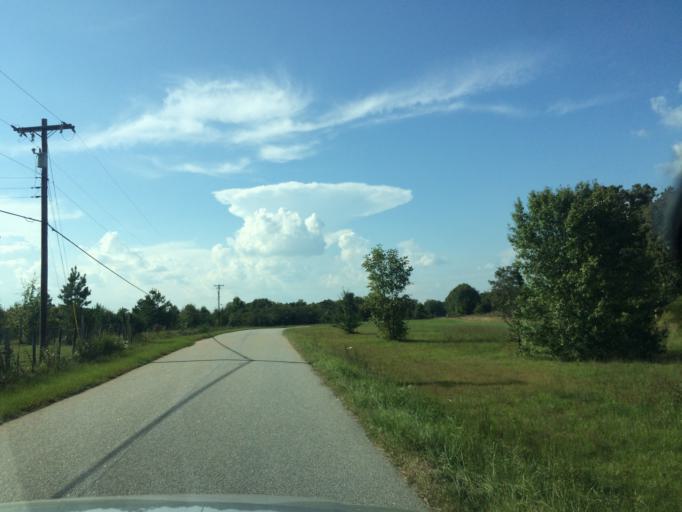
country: US
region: South Carolina
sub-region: Laurens County
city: Laurens
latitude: 34.5807
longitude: -82.0995
